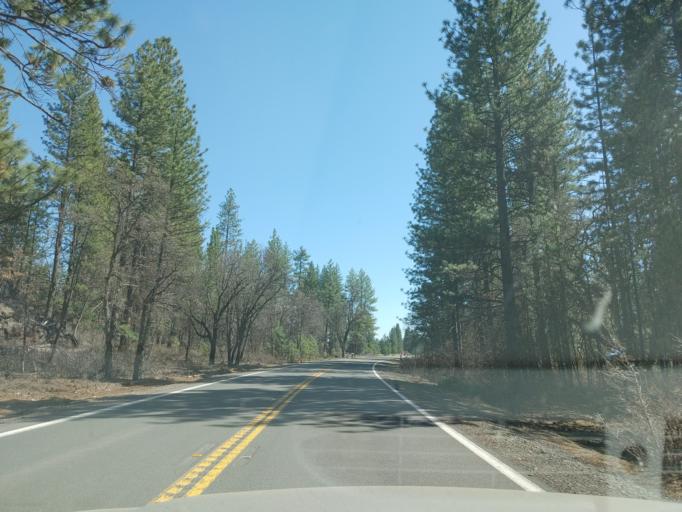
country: US
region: California
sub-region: Shasta County
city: Burney
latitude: 41.0052
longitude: -121.6330
